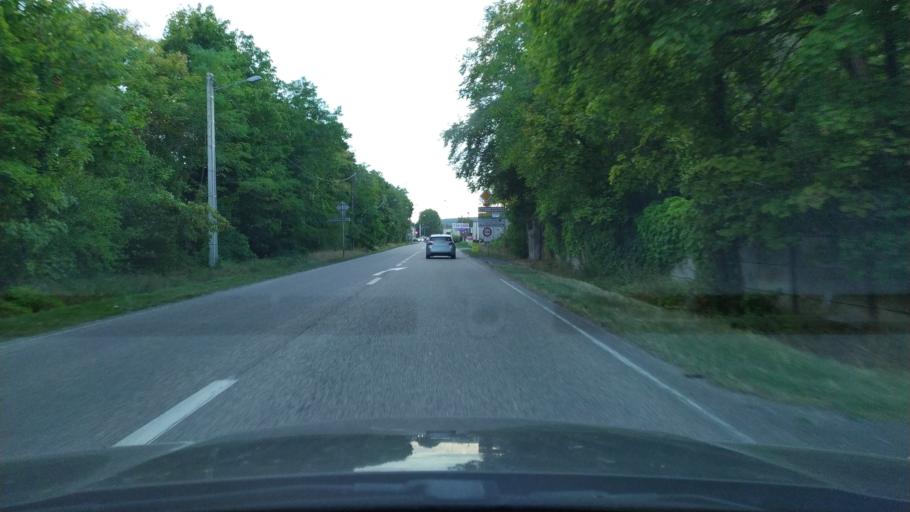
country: FR
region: Lorraine
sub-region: Departement de la Moselle
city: Ars-sur-Moselle
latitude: 49.0866
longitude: 6.0899
